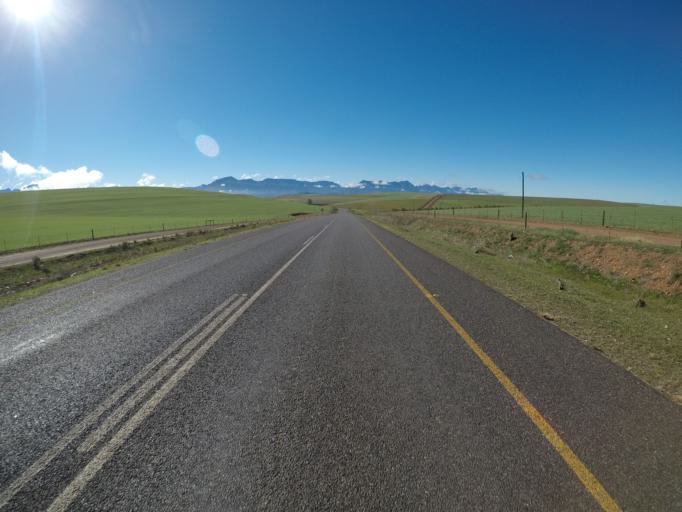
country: ZA
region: Western Cape
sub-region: Overberg District Municipality
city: Caledon
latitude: -34.1406
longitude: 19.5027
